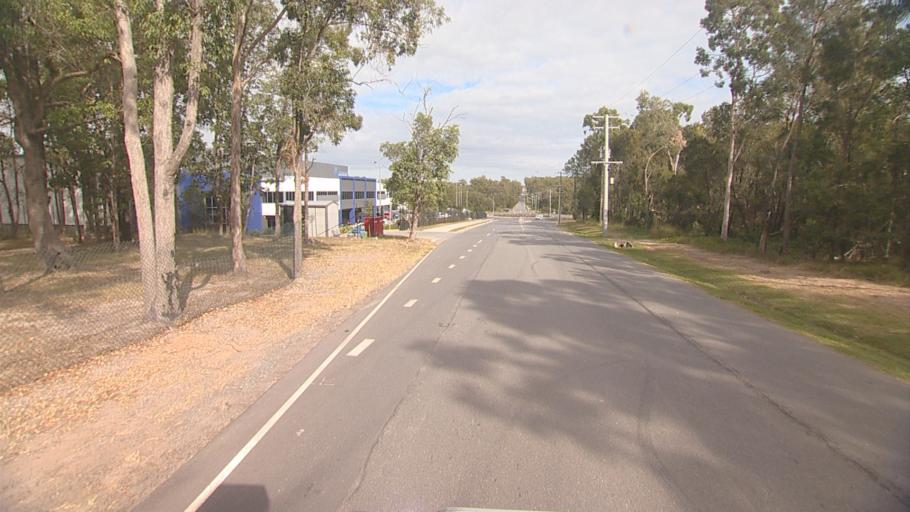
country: AU
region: Queensland
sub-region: Logan
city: Woodridge
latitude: -27.6515
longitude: 153.0901
